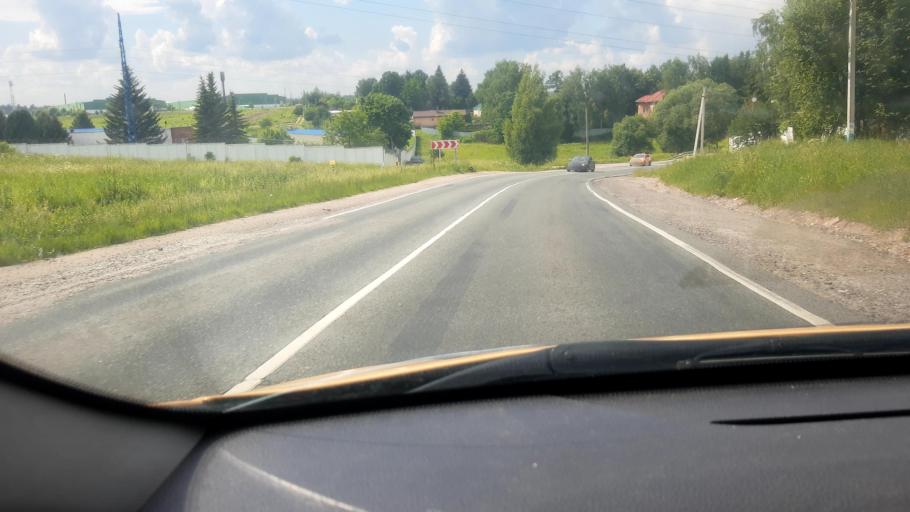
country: RU
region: Moskovskaya
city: Troitsk
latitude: 55.4999
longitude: 37.2884
